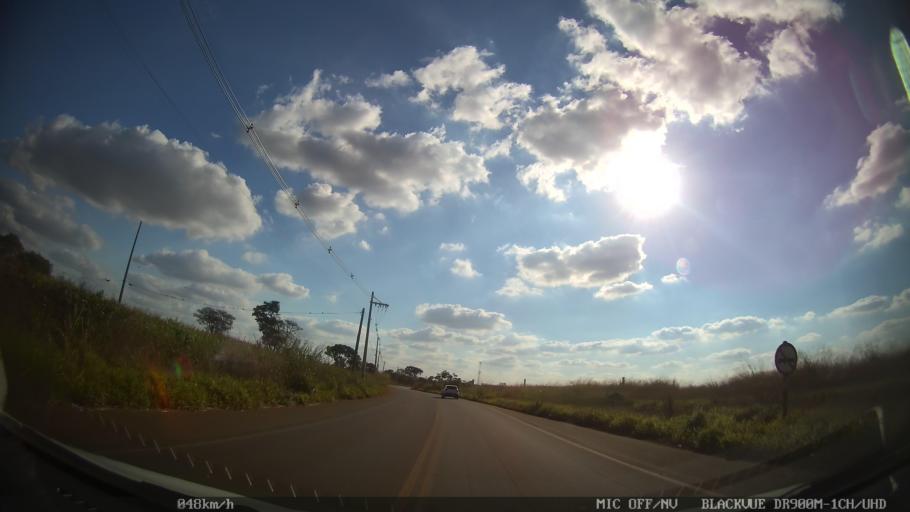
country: BR
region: Sao Paulo
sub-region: Santa Barbara D'Oeste
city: Santa Barbara d'Oeste
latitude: -22.7814
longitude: -47.3670
